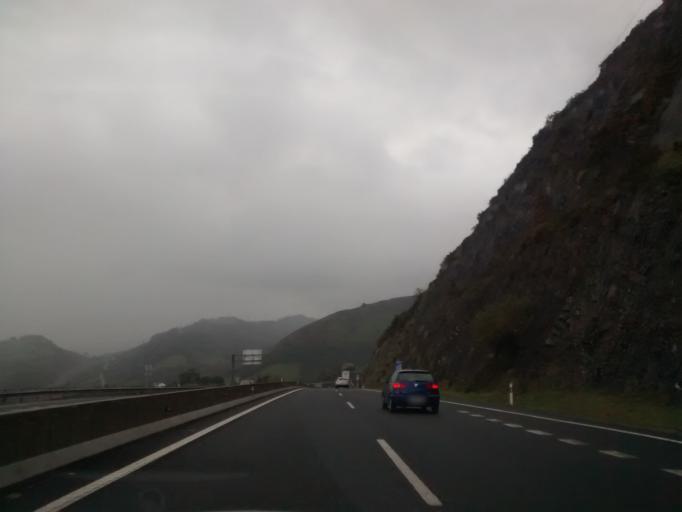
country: ES
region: Cantabria
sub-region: Provincia de Cantabria
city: Castro-Urdiales
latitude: 43.3594
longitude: -3.1854
